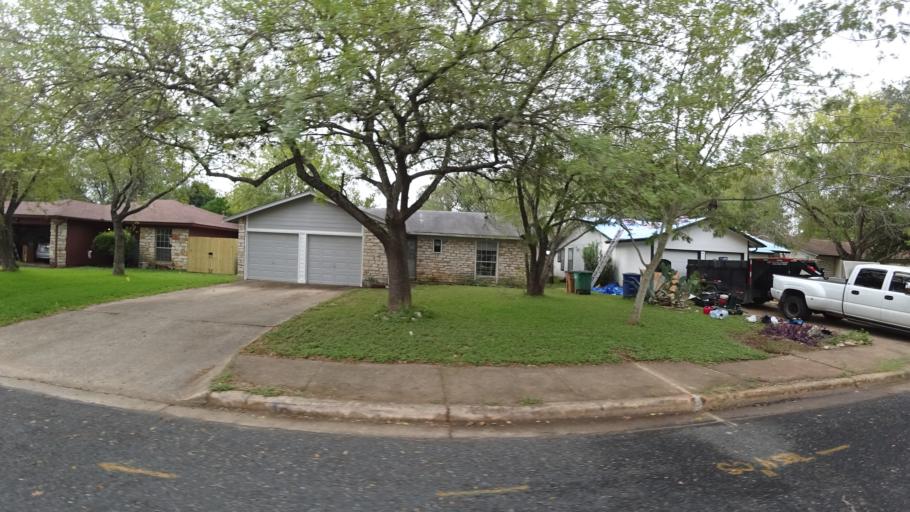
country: US
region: Texas
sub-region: Travis County
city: Shady Hollow
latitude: 30.2119
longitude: -97.8368
